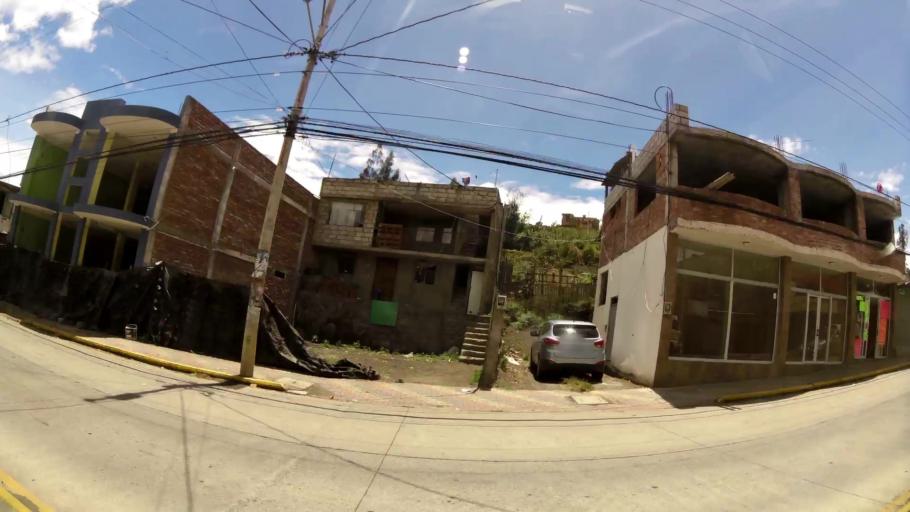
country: EC
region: Tungurahua
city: Pelileo
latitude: -1.3330
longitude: -78.5567
